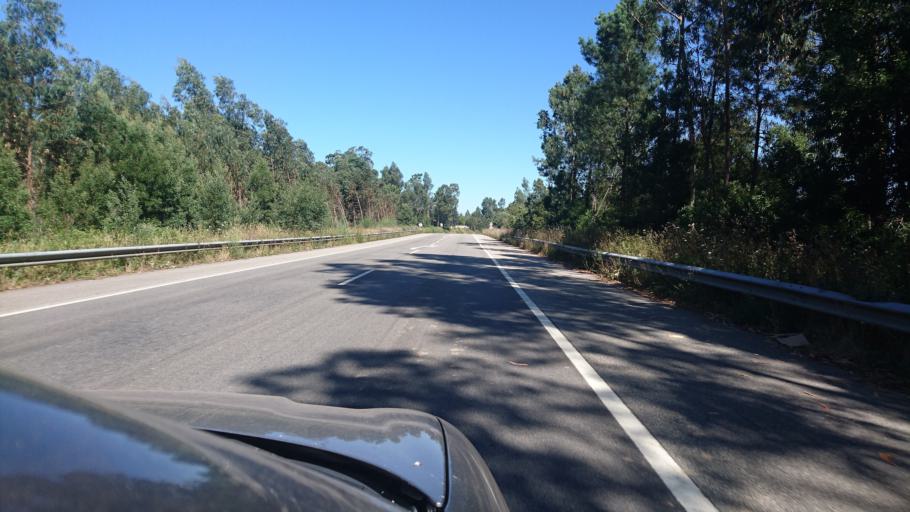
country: PT
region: Aveiro
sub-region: Santa Maria da Feira
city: Rio Meao
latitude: 40.9448
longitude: -8.5861
